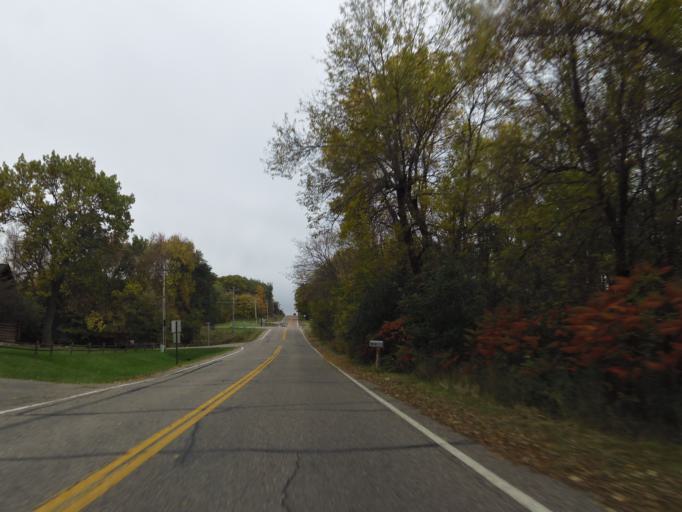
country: US
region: Minnesota
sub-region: Scott County
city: Prior Lake
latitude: 44.6963
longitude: -93.4603
